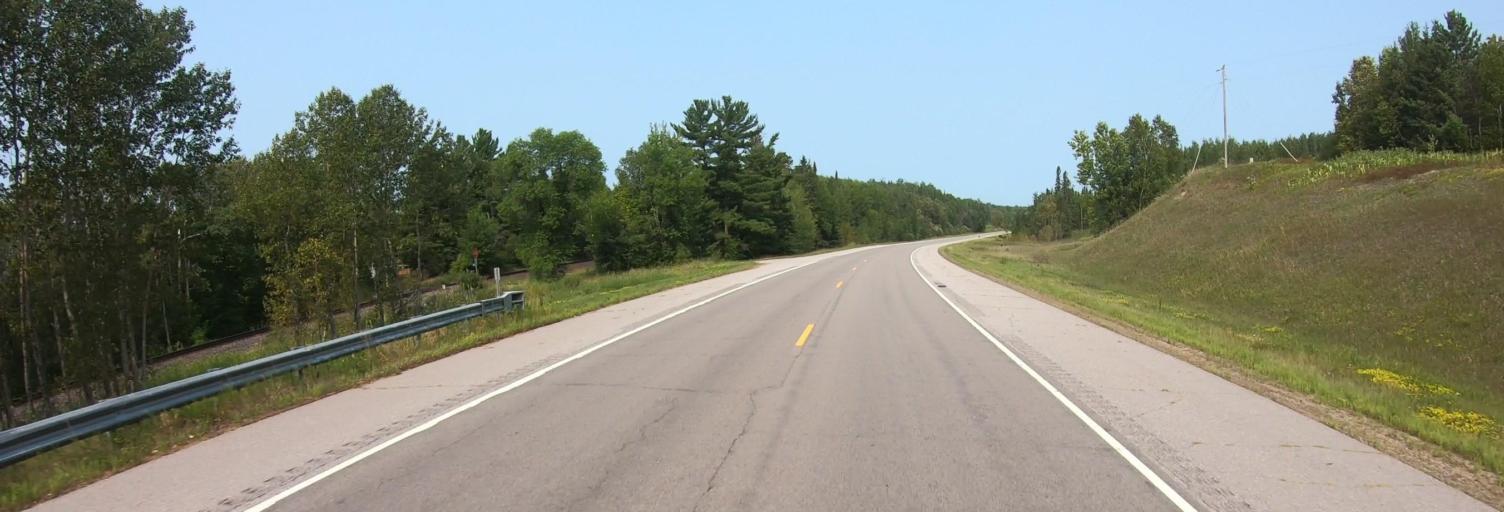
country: CA
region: Ontario
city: Fort Frances
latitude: 48.2211
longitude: -92.9197
